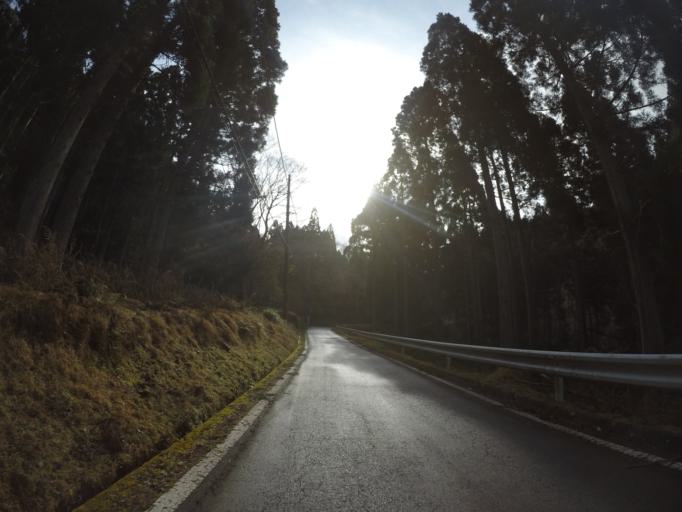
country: JP
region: Shizuoka
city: Heda
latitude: 34.8780
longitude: 138.8574
